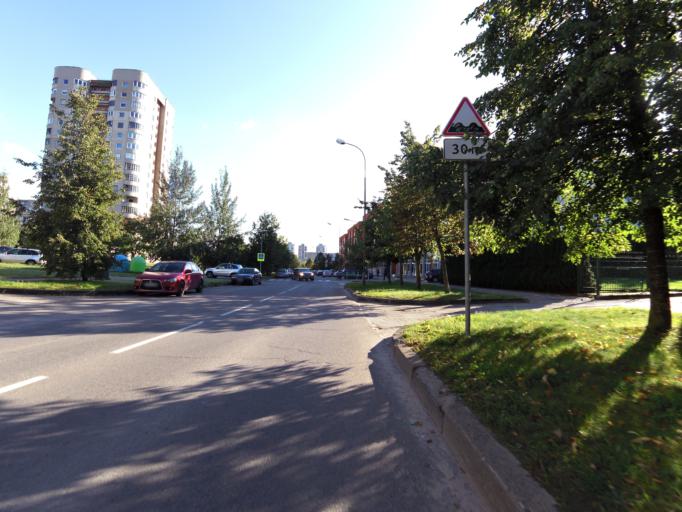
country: LT
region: Vilnius County
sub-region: Vilnius
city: Fabijoniskes
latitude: 54.7255
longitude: 25.2448
